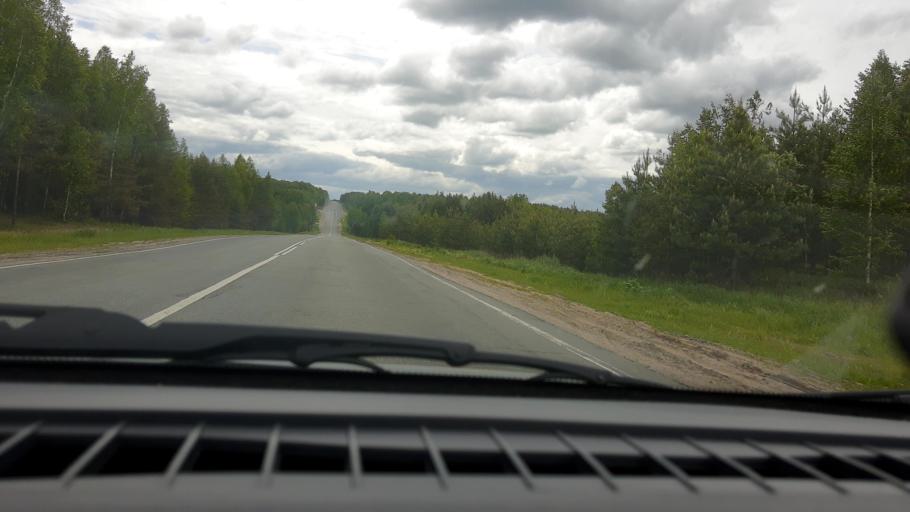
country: RU
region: Nizjnij Novgorod
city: Krasnyye Baki
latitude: 56.9791
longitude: 45.1152
